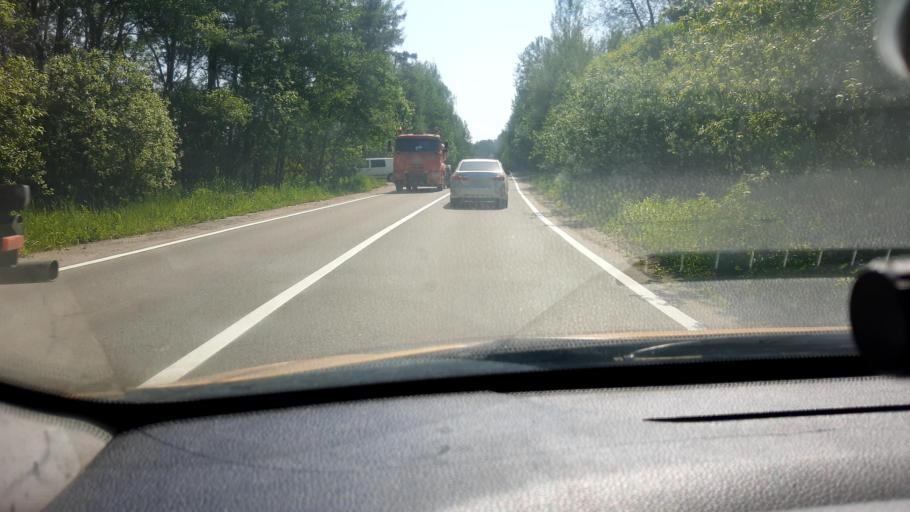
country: RU
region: Moskovskaya
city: Yakovlevskoye
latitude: 55.4552
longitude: 37.8864
